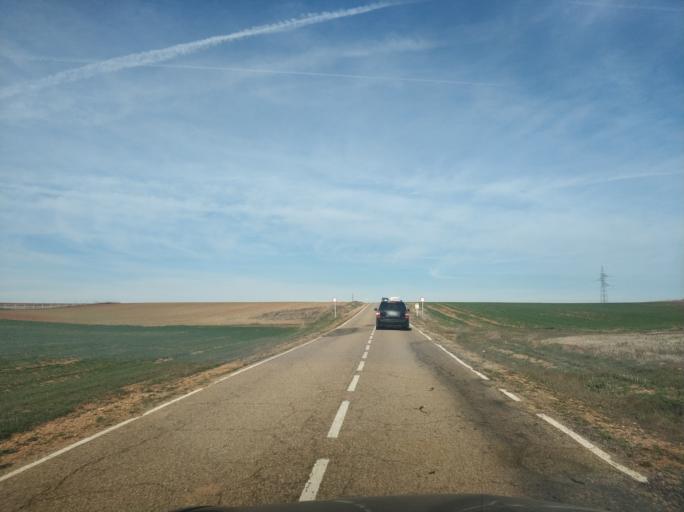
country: ES
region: Castille and Leon
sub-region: Provincia de Salamanca
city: Parada de Arriba
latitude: 40.9925
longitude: -5.8060
